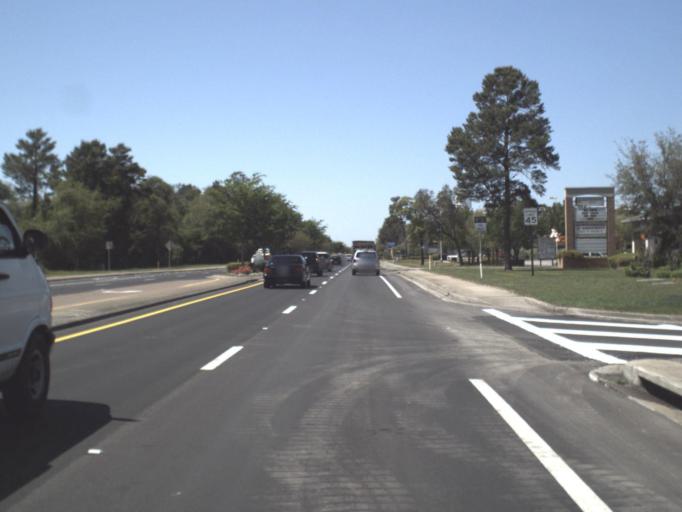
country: US
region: Florida
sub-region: Okaloosa County
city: Niceville
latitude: 30.4844
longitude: -86.4175
